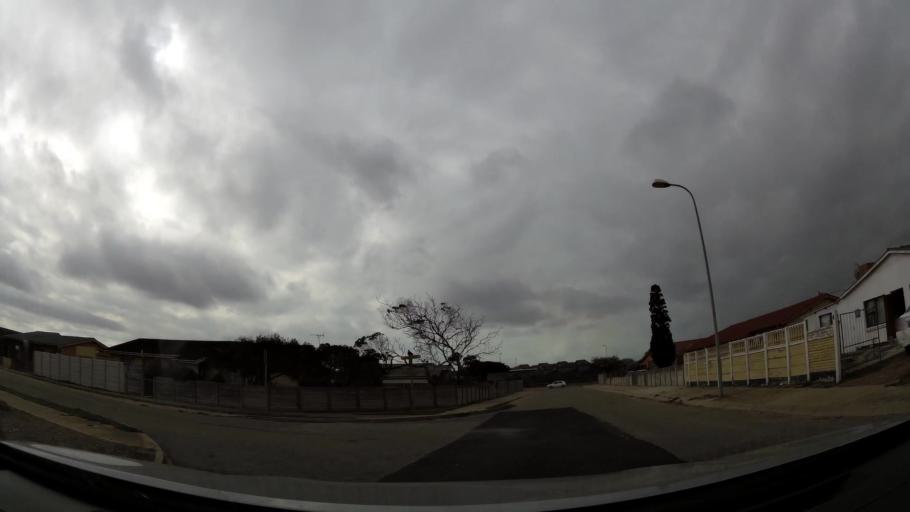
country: ZA
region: Eastern Cape
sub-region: Nelson Mandela Bay Metropolitan Municipality
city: Port Elizabeth
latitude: -33.8939
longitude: 25.5638
